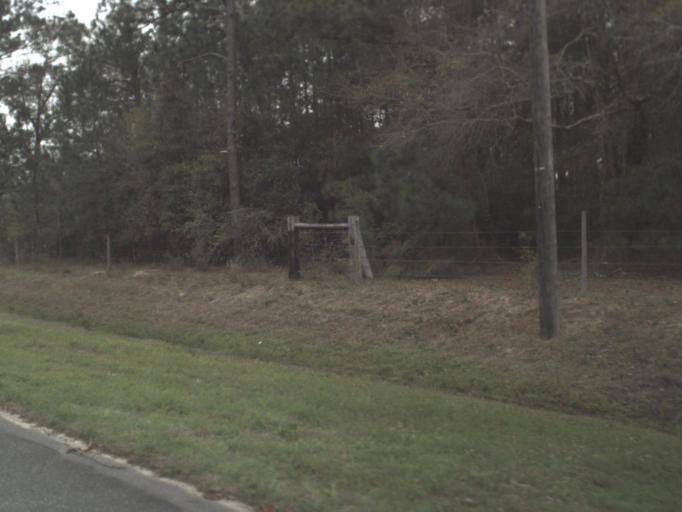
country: US
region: Florida
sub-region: Liberty County
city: Bristol
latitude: 30.4069
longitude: -84.7851
